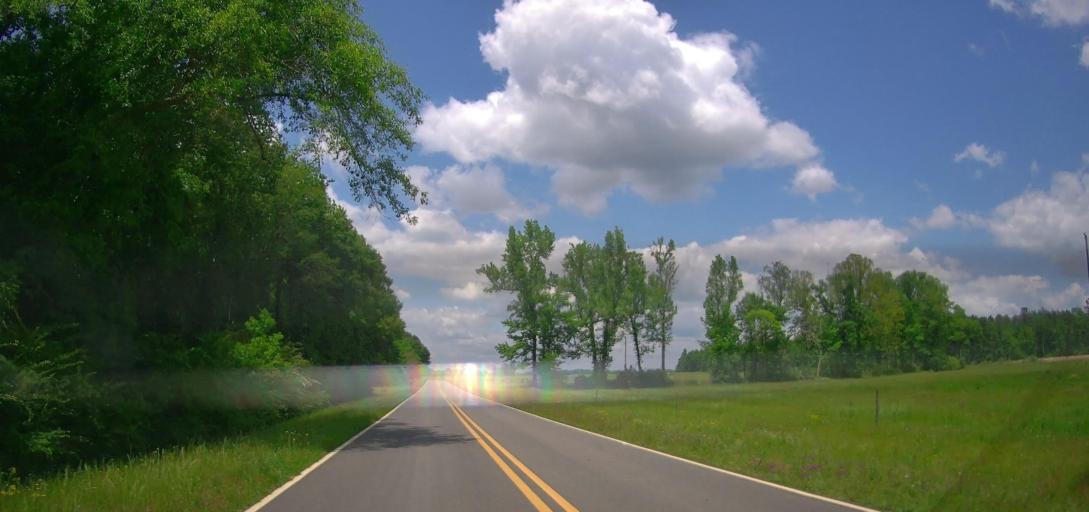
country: US
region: Georgia
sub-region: Laurens County
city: East Dublin
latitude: 32.6275
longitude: -82.8339
